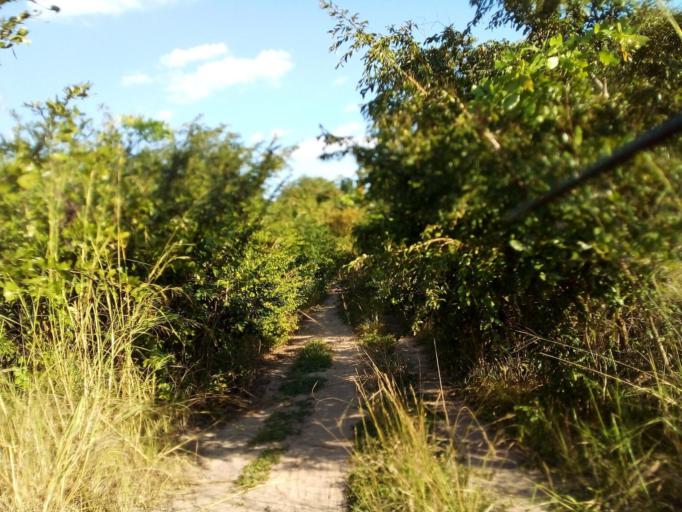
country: MZ
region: Zambezia
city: Quelimane
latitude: -17.5429
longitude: 36.8566
